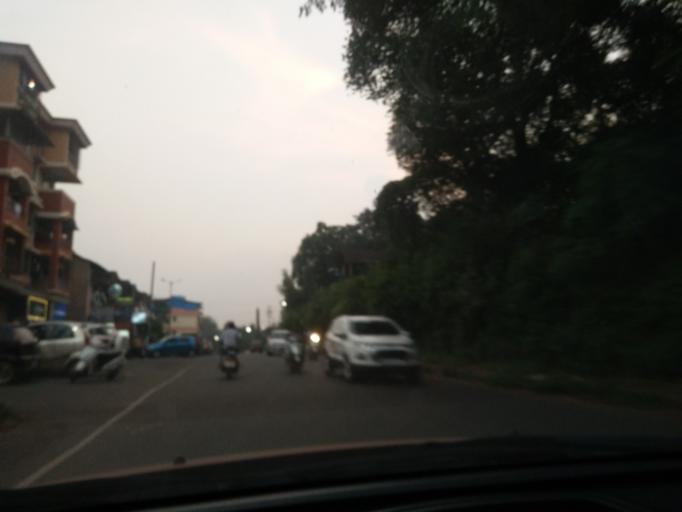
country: IN
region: Goa
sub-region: South Goa
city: Madgaon
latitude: 15.2769
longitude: 73.9748
